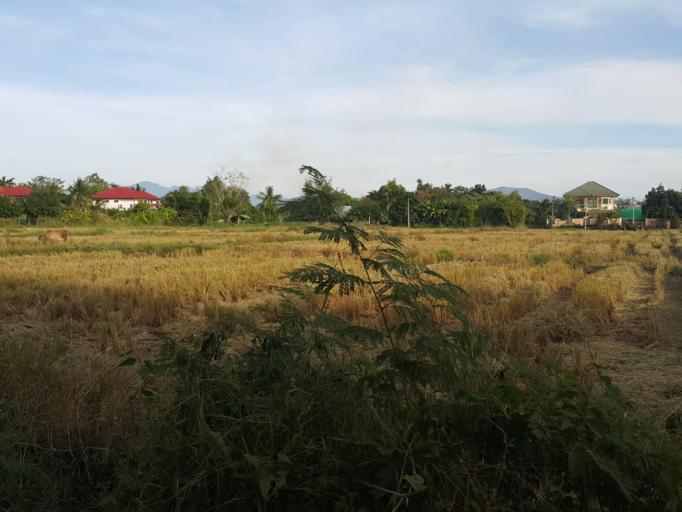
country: TH
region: Chiang Mai
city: San Kamphaeng
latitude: 18.8259
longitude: 99.1387
